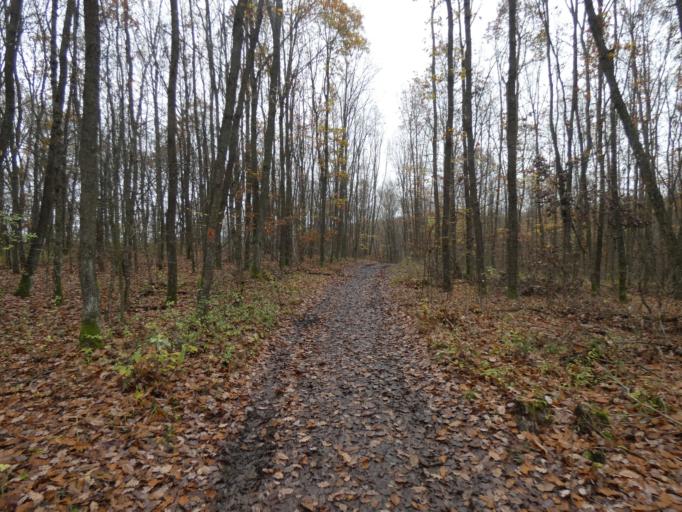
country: HU
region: Pest
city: Kismaros
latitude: 47.8953
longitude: 18.9841
